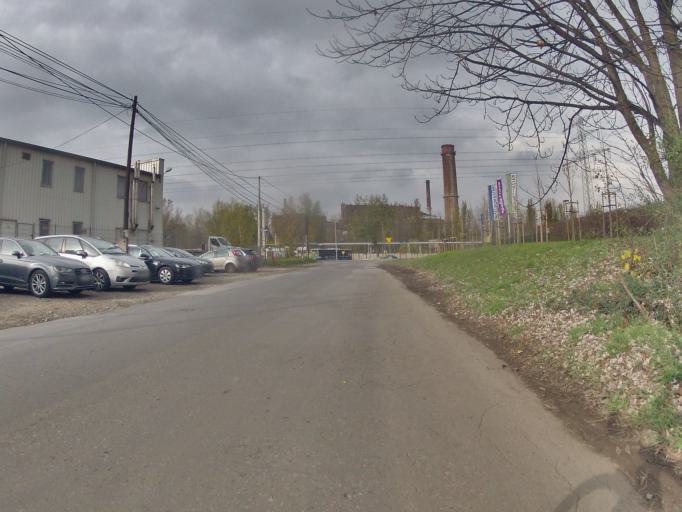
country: PL
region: Lesser Poland Voivodeship
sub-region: Powiat wielicki
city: Wegrzce Wielkie
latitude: 50.0693
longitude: 20.1011
